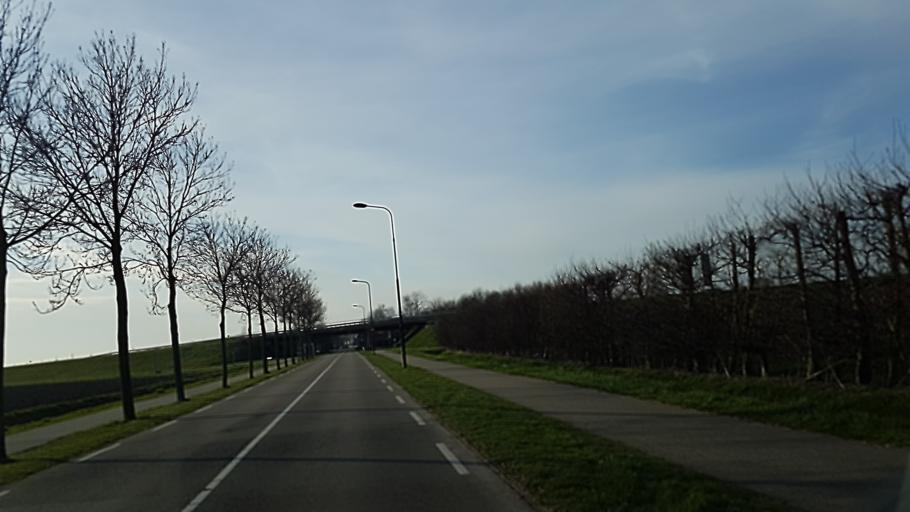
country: NL
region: Zeeland
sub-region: Gemeente Tholen
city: Tholen
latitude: 51.4204
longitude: 4.1686
